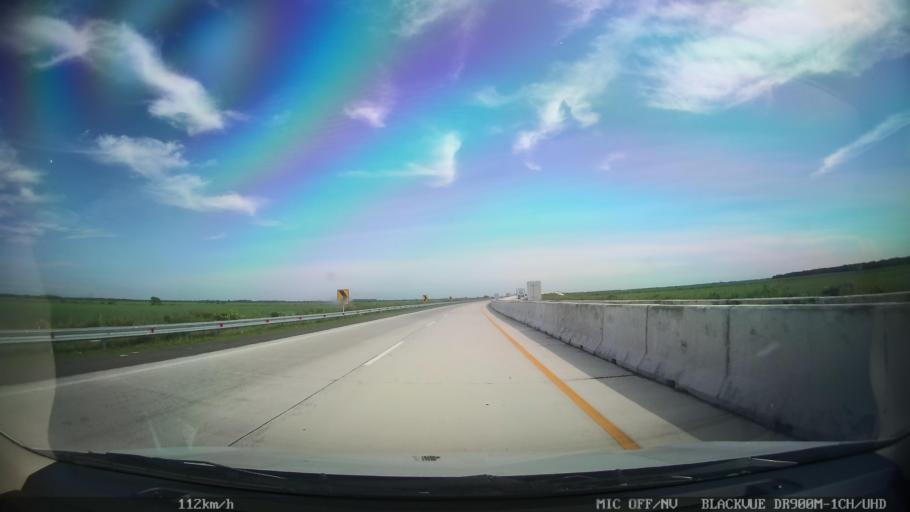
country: ID
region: North Sumatra
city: Binjai
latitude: 3.6591
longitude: 98.5323
